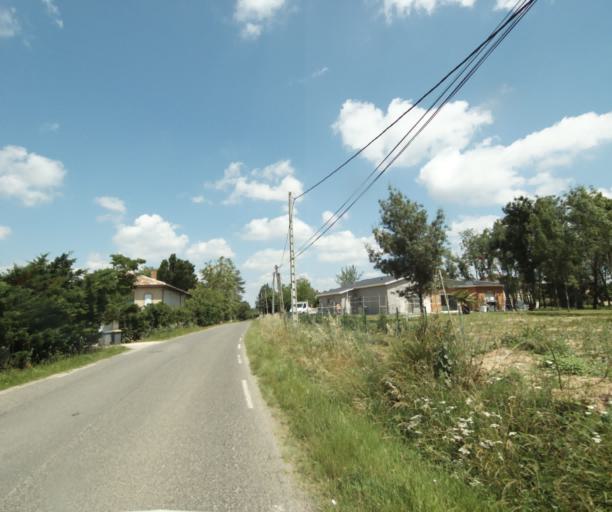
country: FR
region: Midi-Pyrenees
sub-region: Departement du Tarn-et-Garonne
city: Montauban
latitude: 44.0477
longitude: 1.3443
